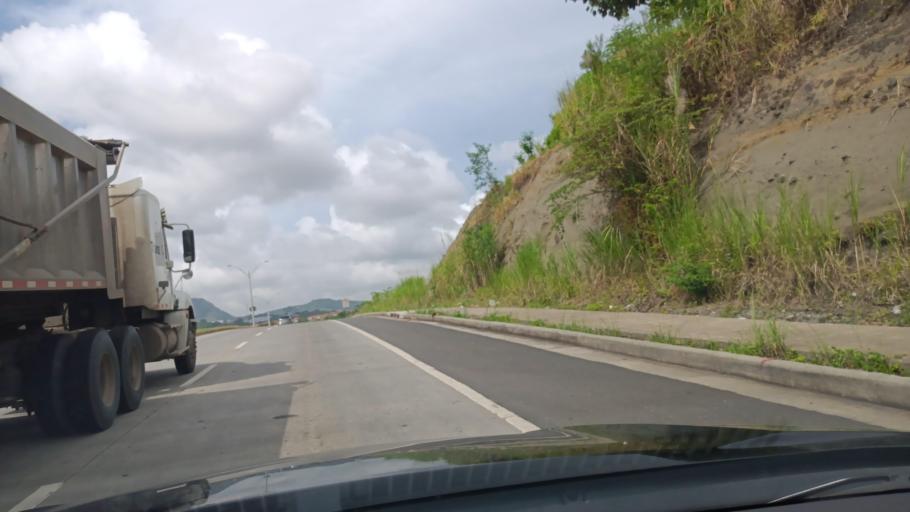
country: PA
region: Panama
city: Las Cumbres
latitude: 9.0988
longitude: -79.5108
